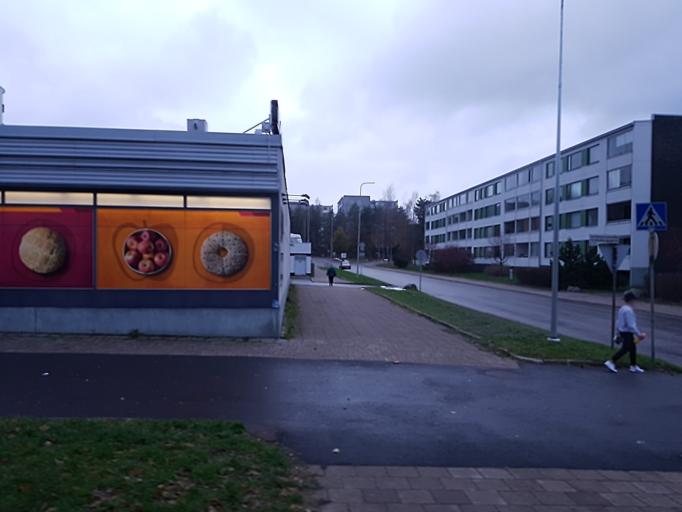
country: FI
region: Varsinais-Suomi
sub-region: Turku
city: Turku
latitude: 60.4736
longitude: 22.2496
